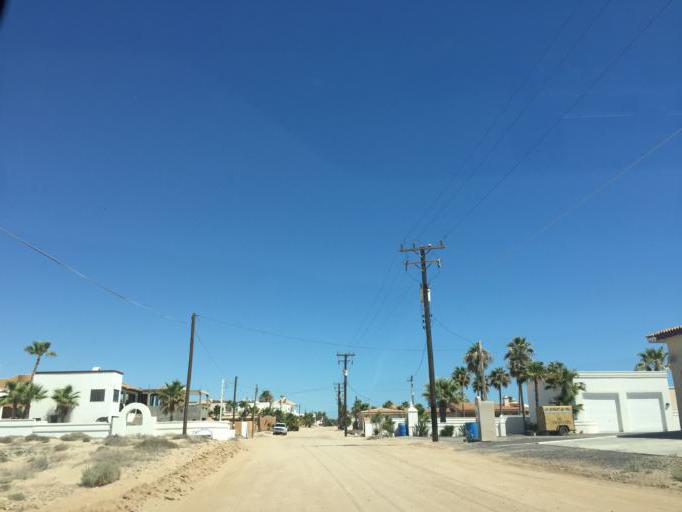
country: MX
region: Sonora
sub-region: Puerto Penasco
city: Puerto Penasco
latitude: 31.2938
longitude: -113.5181
